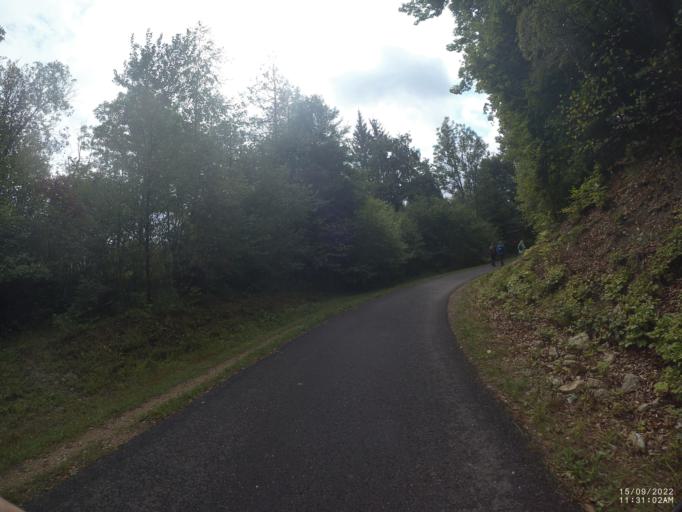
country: DE
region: Rheinland-Pfalz
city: Nohn
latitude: 50.3213
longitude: 6.7760
